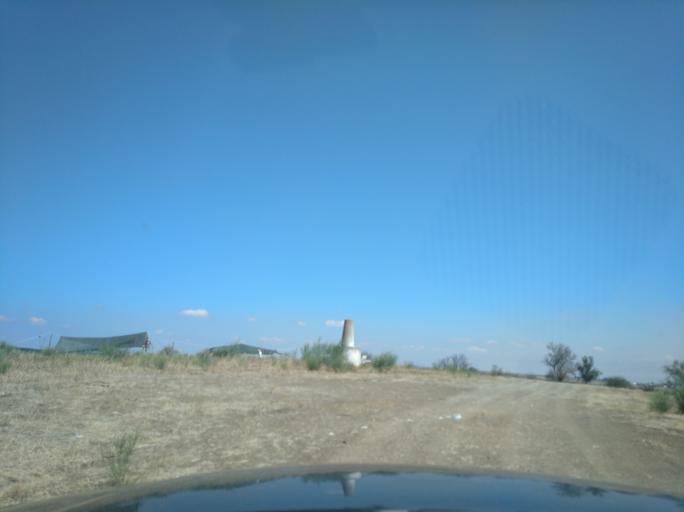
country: PT
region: Portalegre
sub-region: Campo Maior
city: Campo Maior
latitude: 39.0039
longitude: -7.0919
